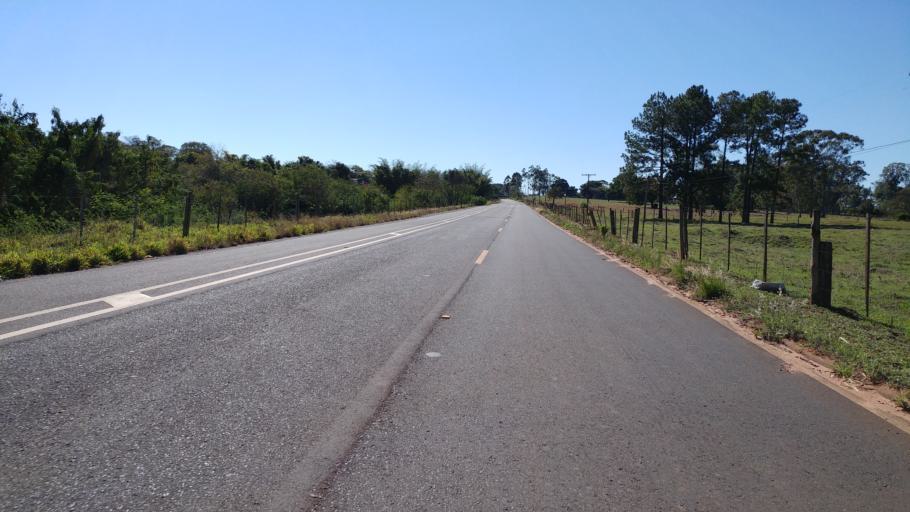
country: BR
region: Sao Paulo
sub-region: Paraguacu Paulista
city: Paraguacu Paulista
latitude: -22.4194
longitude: -50.5993
